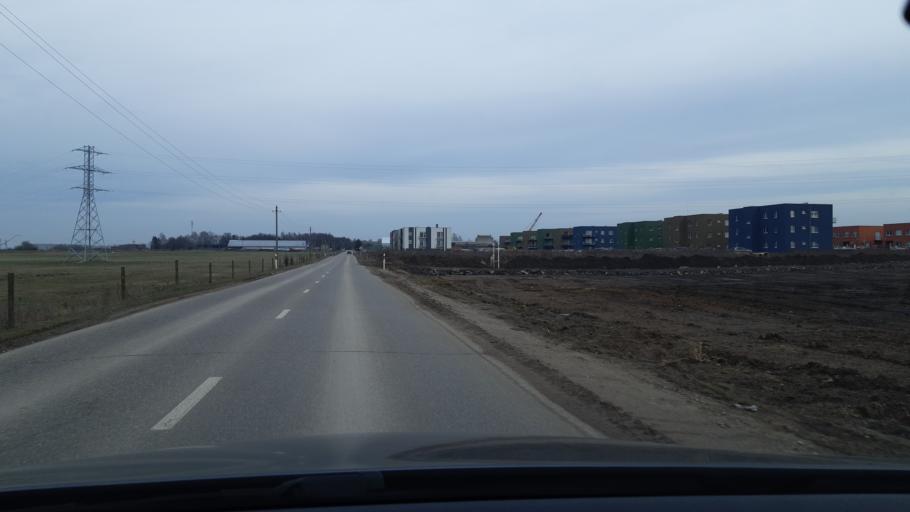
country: LT
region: Kauno apskritis
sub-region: Kaunas
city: Sargenai
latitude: 54.9524
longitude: 23.8513
